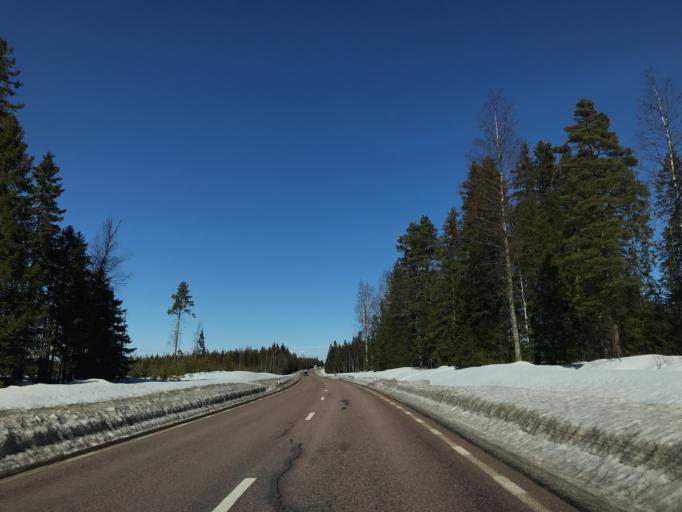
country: SE
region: Dalarna
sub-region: Vansbro Kommun
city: Vansbro
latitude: 60.3860
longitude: 14.2088
